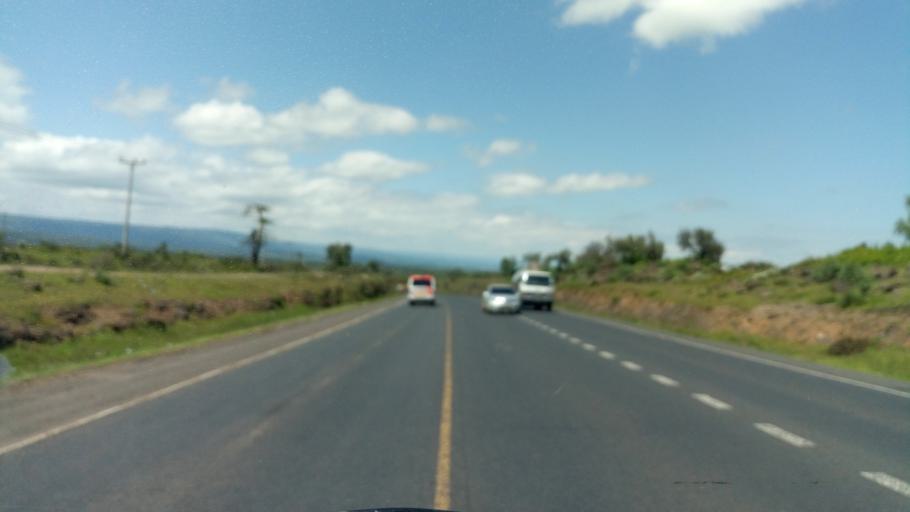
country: KE
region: Nakuru
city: Naivasha
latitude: -0.5410
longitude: 36.3379
